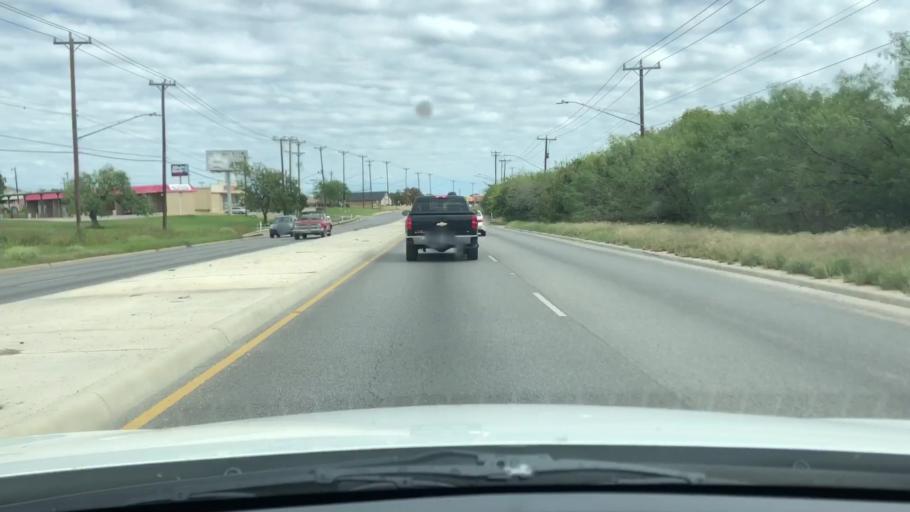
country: US
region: Texas
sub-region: Bexar County
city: Leon Valley
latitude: 29.4903
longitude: -98.6873
